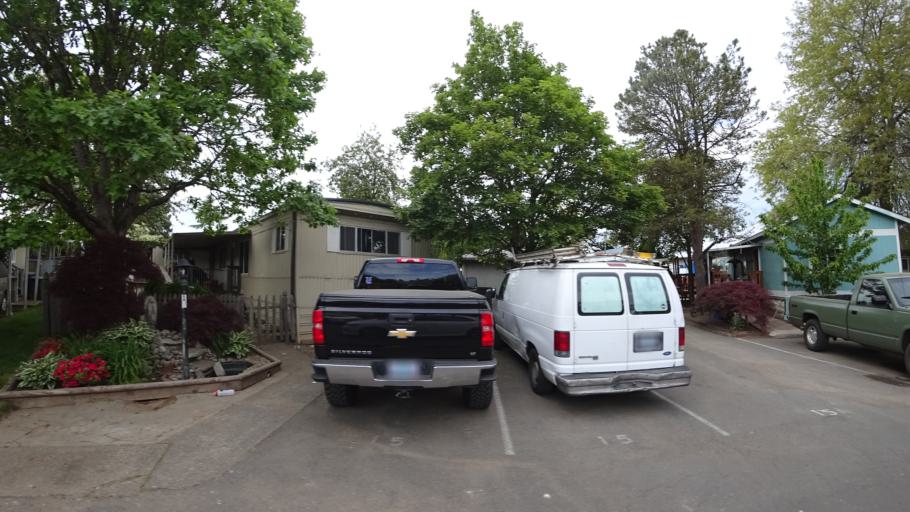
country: US
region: Oregon
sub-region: Washington County
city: Hillsboro
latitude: 45.5014
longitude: -122.9527
